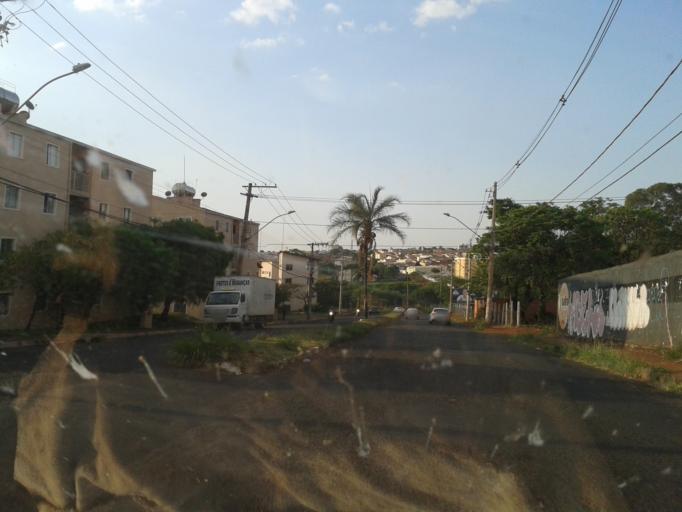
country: BR
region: Minas Gerais
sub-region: Uberlandia
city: Uberlandia
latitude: -18.9239
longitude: -48.3216
